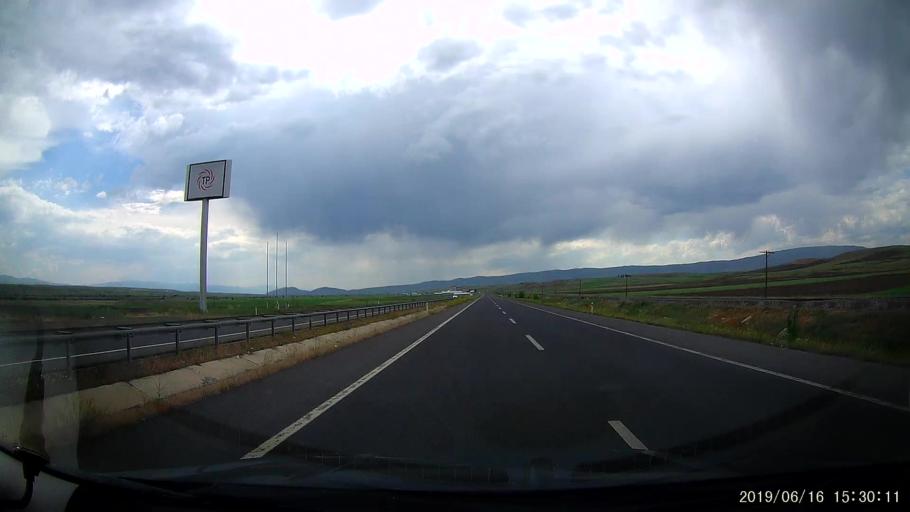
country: TR
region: Erzurum
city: Horasan
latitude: 40.0332
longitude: 42.1127
